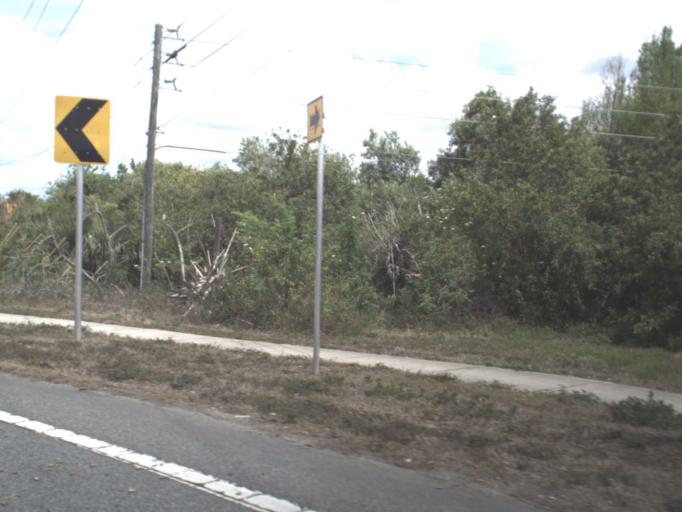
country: US
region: Florida
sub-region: Brevard County
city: Cocoa
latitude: 28.3970
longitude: -80.7552
